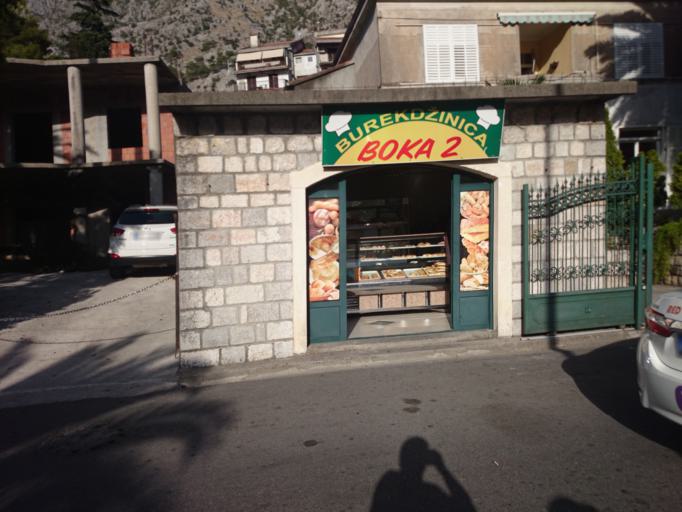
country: ME
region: Kotor
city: Kotor
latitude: 42.4295
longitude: 18.7682
